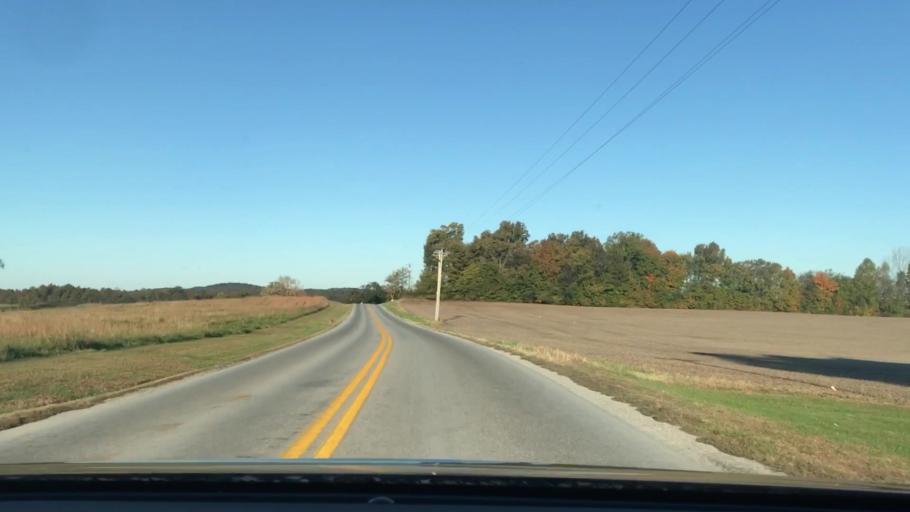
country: US
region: Kentucky
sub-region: Logan County
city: Auburn
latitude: 36.8460
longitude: -86.6992
